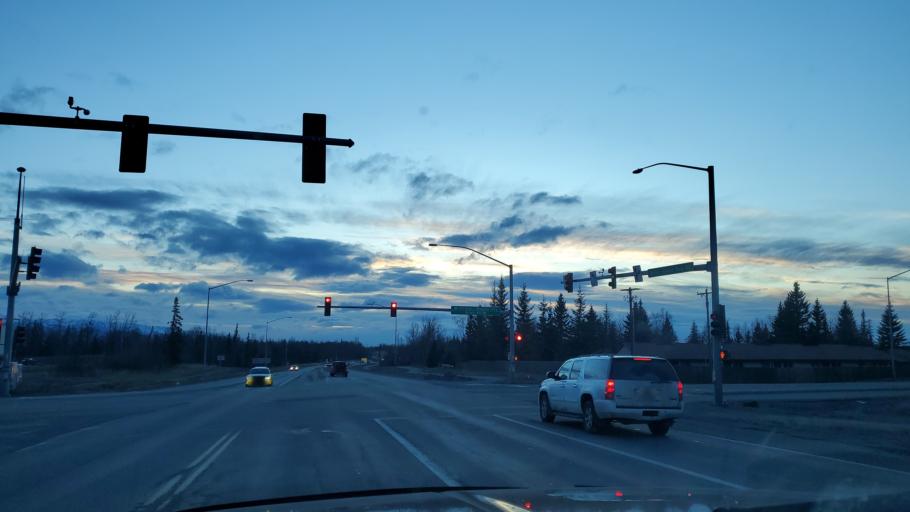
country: US
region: Alaska
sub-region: Matanuska-Susitna Borough
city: Wasilla
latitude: 61.5709
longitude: -149.4446
